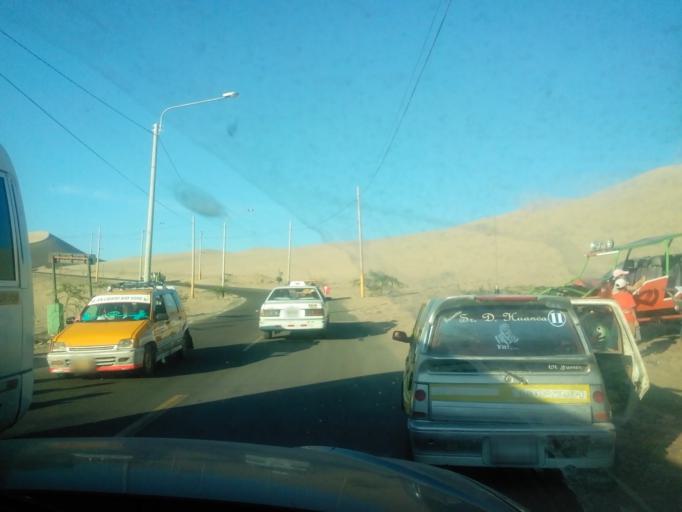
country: PE
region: Ica
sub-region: Provincia de Ica
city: Ica
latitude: -14.0882
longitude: -75.7612
